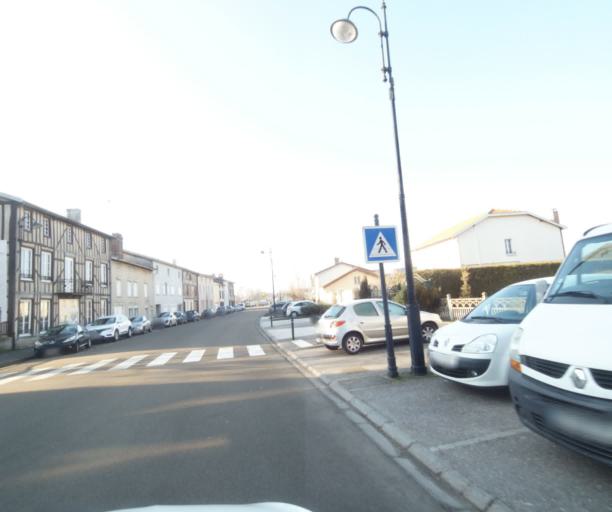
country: FR
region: Champagne-Ardenne
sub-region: Departement de la Haute-Marne
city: Montier-en-Der
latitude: 48.4756
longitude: 4.7692
